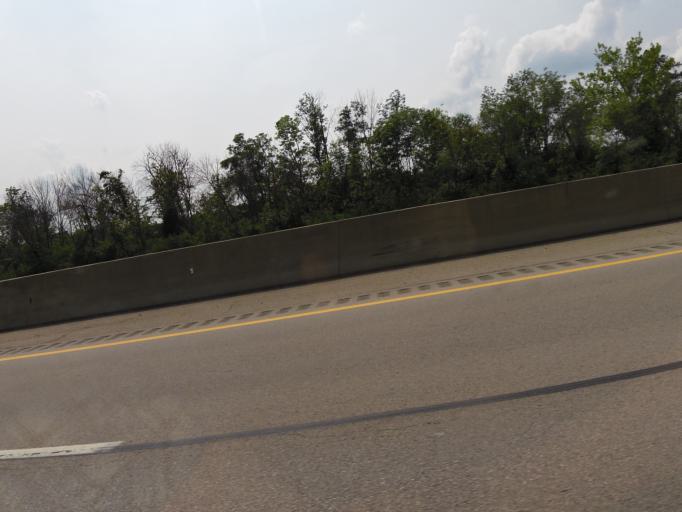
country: US
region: Kentucky
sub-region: Boone County
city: Walton
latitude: 38.8911
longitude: -84.6263
